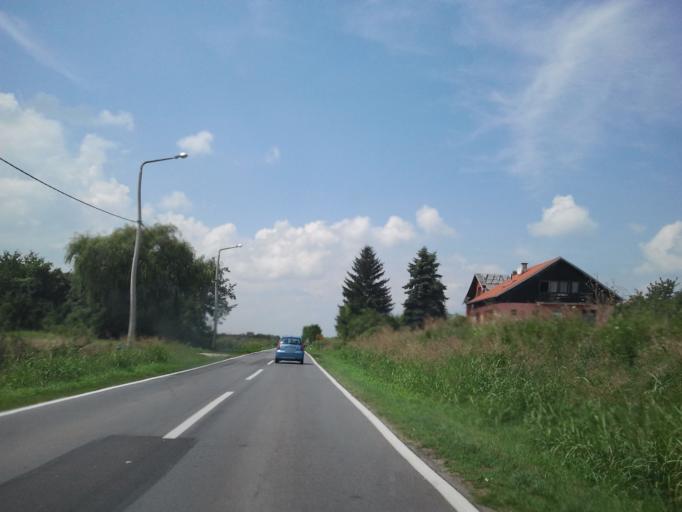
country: HR
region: Vukovarsko-Srijemska
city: Negoslavci
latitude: 45.3037
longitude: 19.0863
